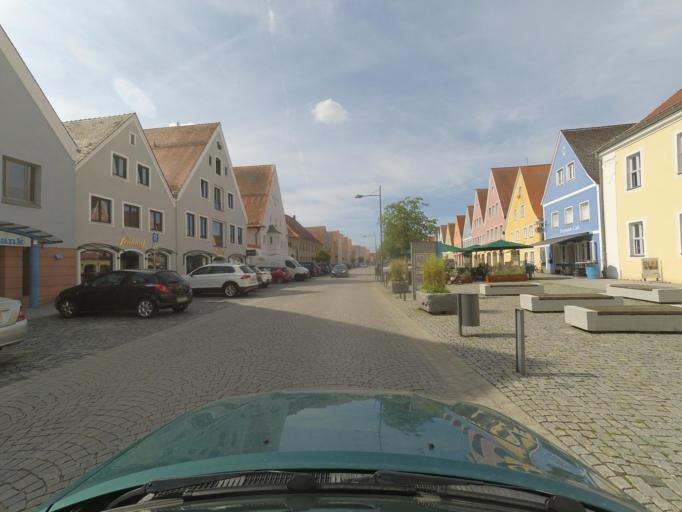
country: DE
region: Bavaria
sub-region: Upper Palatinate
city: Freystadt
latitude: 49.1981
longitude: 11.3303
